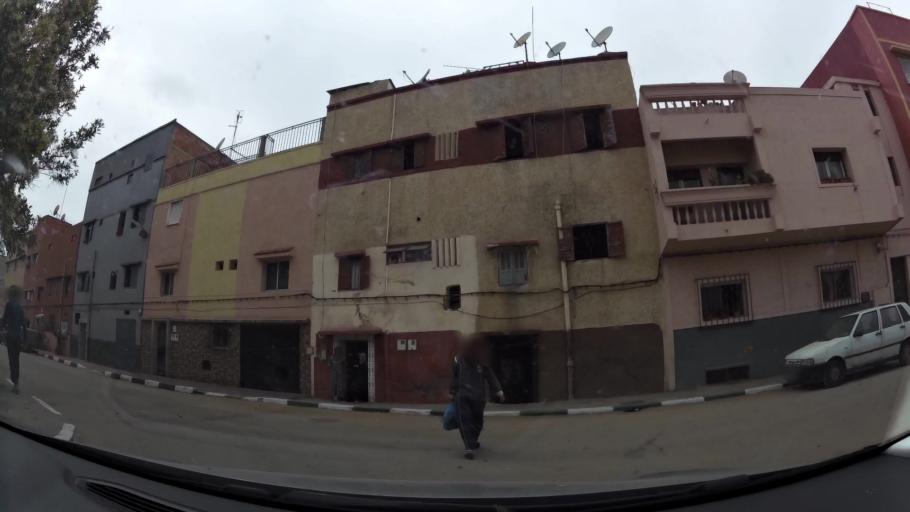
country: MA
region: Rabat-Sale-Zemmour-Zaer
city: Sale
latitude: 34.0331
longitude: -6.8001
